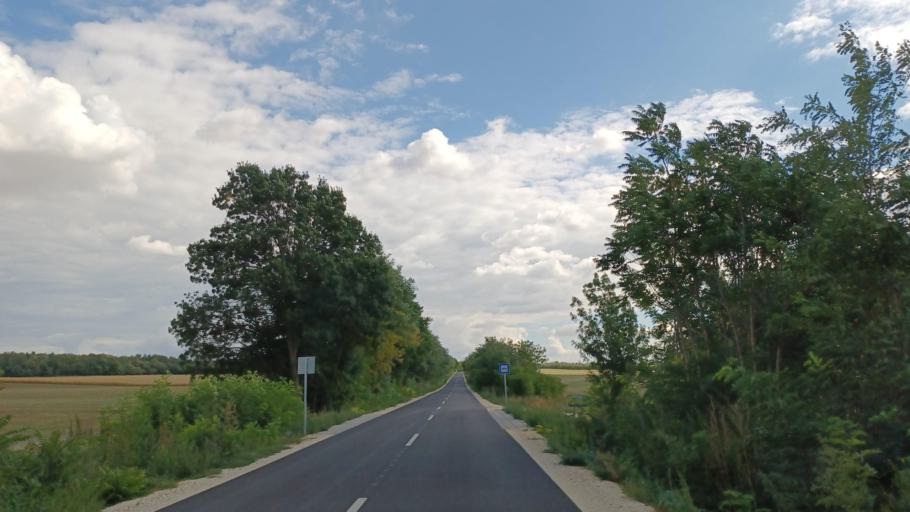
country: HU
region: Tolna
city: Nagydorog
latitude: 46.6060
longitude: 18.6920
